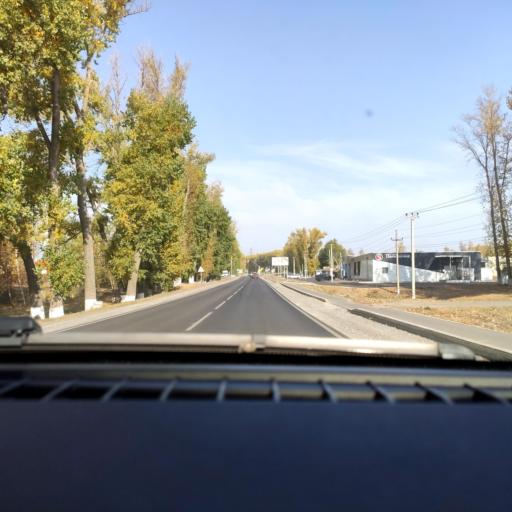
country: RU
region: Voronezj
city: Novaya Usman'
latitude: 51.6680
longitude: 39.4053
